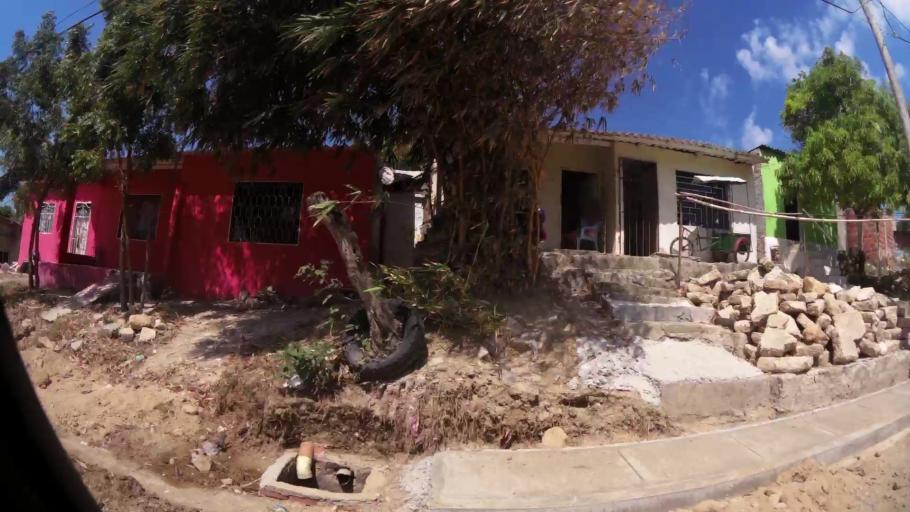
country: CO
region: Atlantico
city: Barranquilla
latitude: 10.9666
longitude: -74.8220
